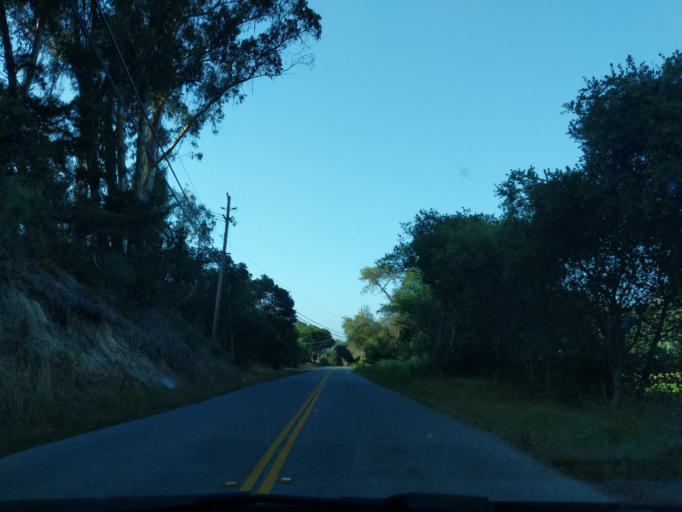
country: US
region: California
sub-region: Monterey County
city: Las Lomas
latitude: 36.8726
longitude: -121.6895
